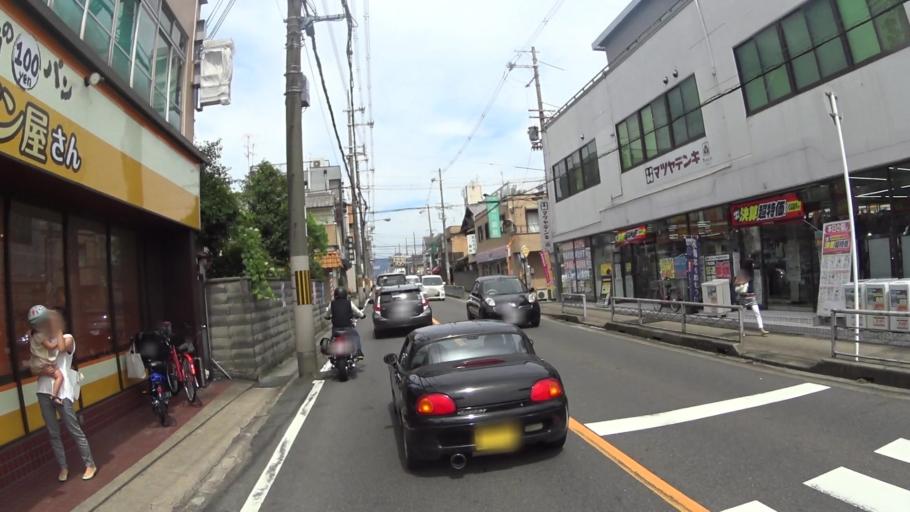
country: JP
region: Kyoto
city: Muko
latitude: 34.9719
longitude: 135.6940
